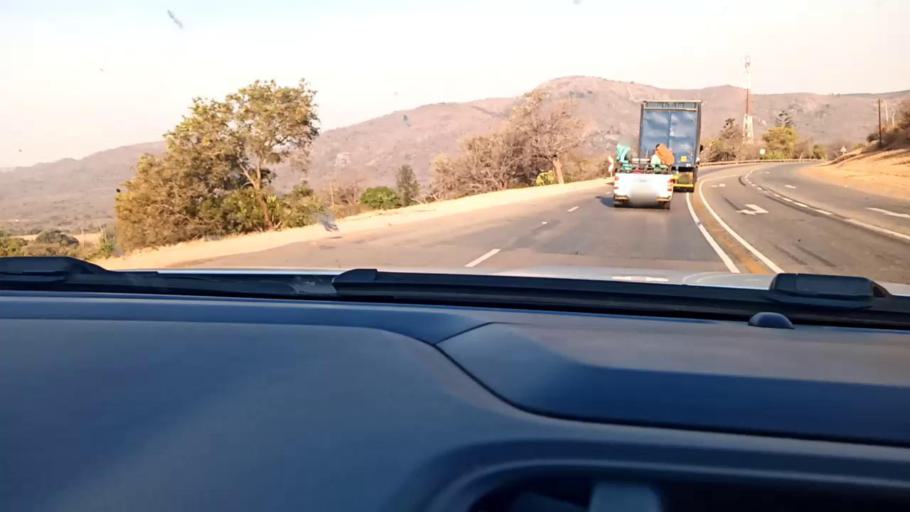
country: ZA
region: Limpopo
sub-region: Mopani District Municipality
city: Ga-Kgapane
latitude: -23.6464
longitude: 30.1690
